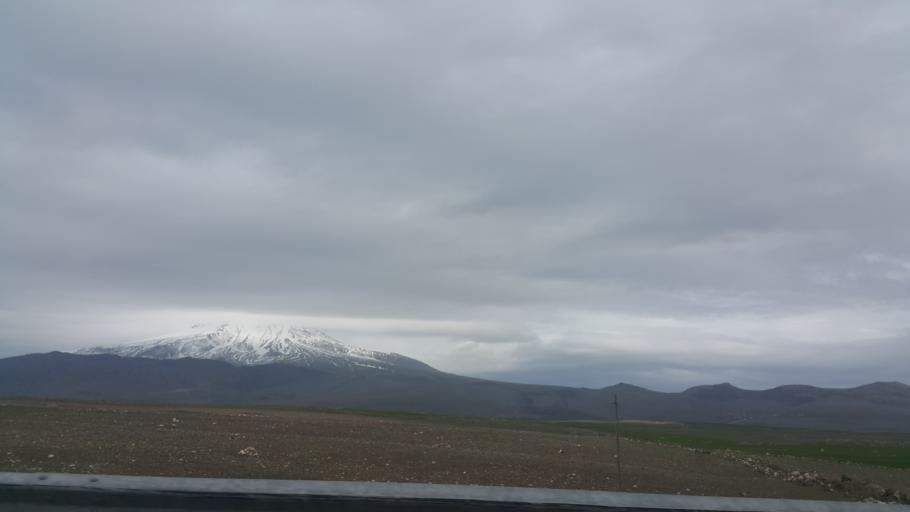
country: TR
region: Aksaray
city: Taspinar
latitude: 38.1024
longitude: 34.0335
